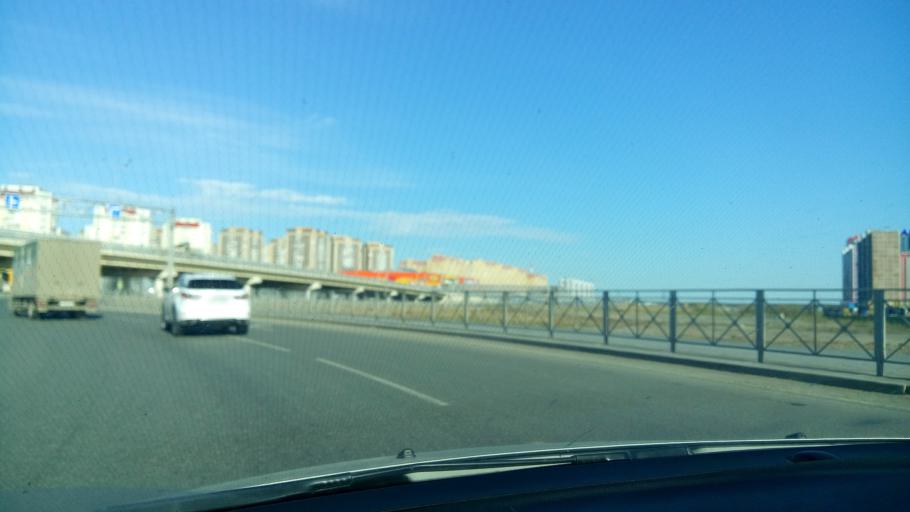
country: RU
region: Tjumen
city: Tyumen
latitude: 57.1040
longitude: 65.5617
